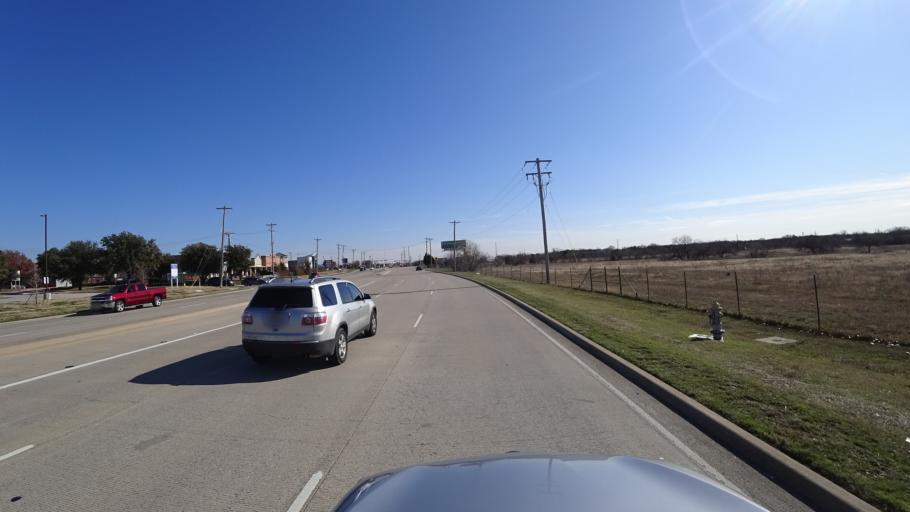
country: US
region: Texas
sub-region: Denton County
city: Lewisville
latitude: 33.0048
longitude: -97.0101
